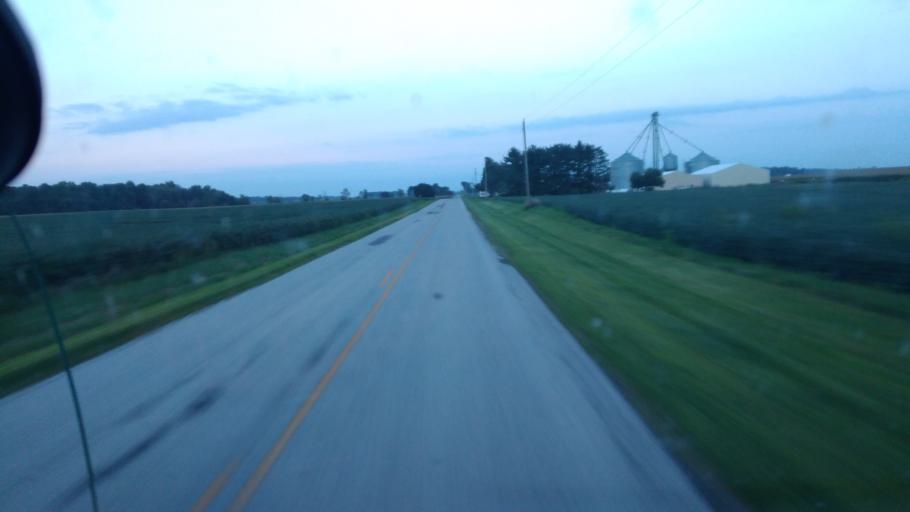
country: US
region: Ohio
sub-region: Hardin County
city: Kenton
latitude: 40.6722
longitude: -83.4933
